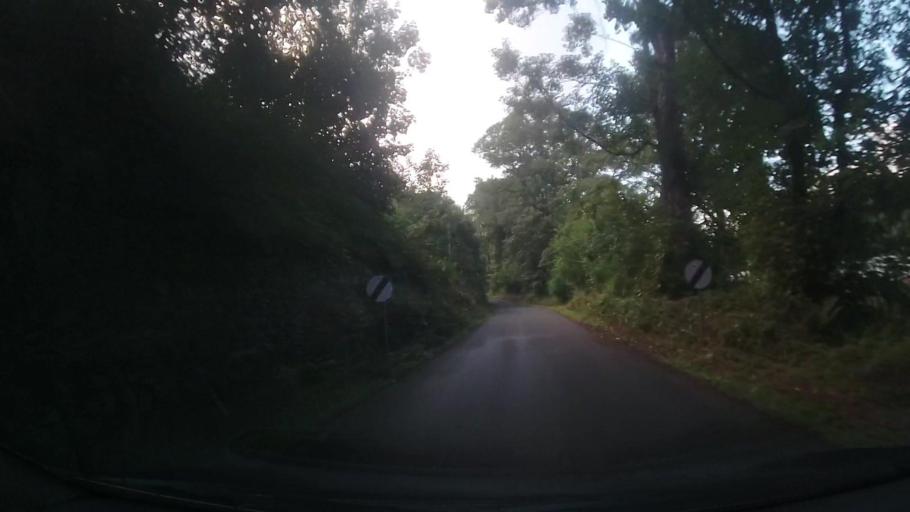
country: GB
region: Wales
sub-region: Pembrokeshire
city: Saundersfoot
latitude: 51.7338
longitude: -4.6562
